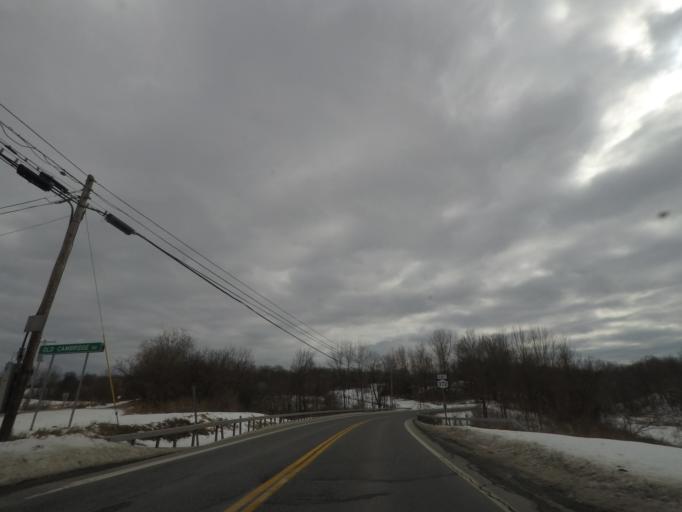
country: US
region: New York
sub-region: Washington County
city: Greenwich
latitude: 43.0824
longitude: -73.4843
